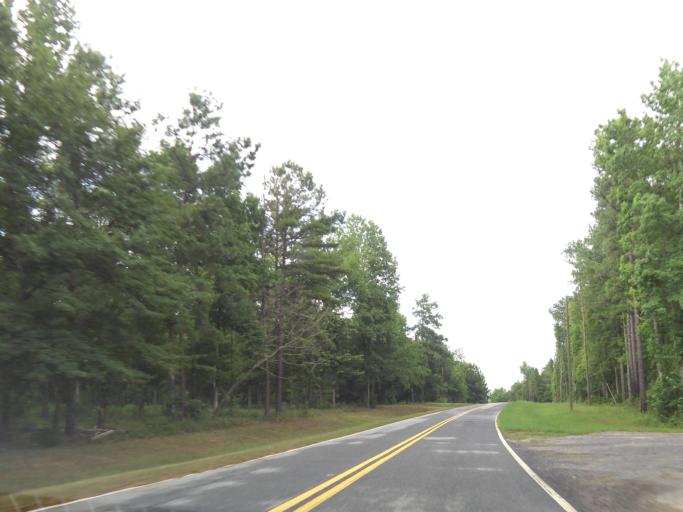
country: US
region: Georgia
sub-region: Bibb County
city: West Point
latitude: 32.8233
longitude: -83.8394
